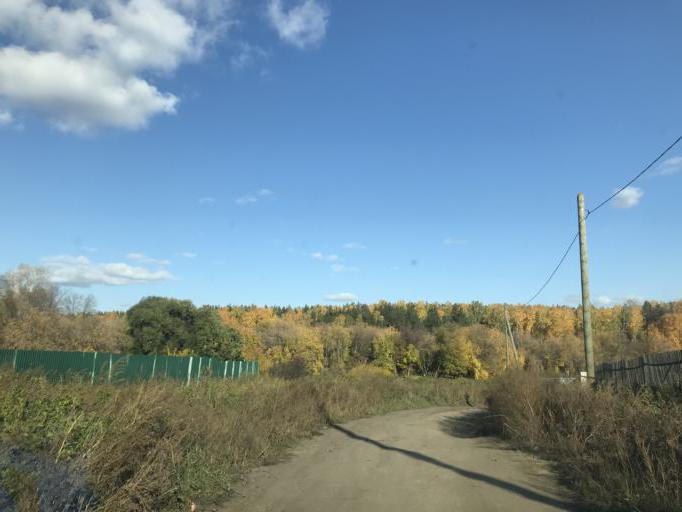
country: RU
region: Chelyabinsk
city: Dolgoderevenskoye
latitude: 55.2757
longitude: 61.3555
